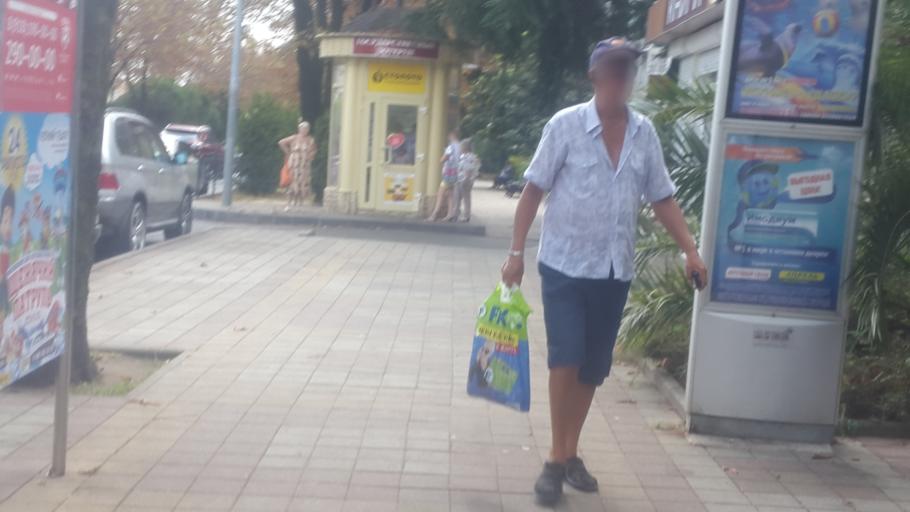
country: RU
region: Krasnodarskiy
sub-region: Sochi City
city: Sochi
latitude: 43.5960
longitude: 39.7227
